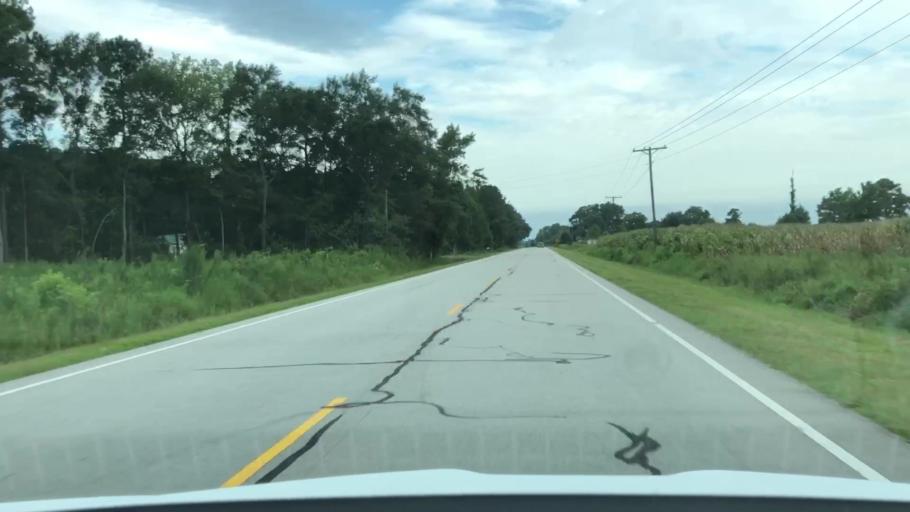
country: US
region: North Carolina
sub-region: Lenoir County
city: Kinston
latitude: 35.1315
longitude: -77.5247
